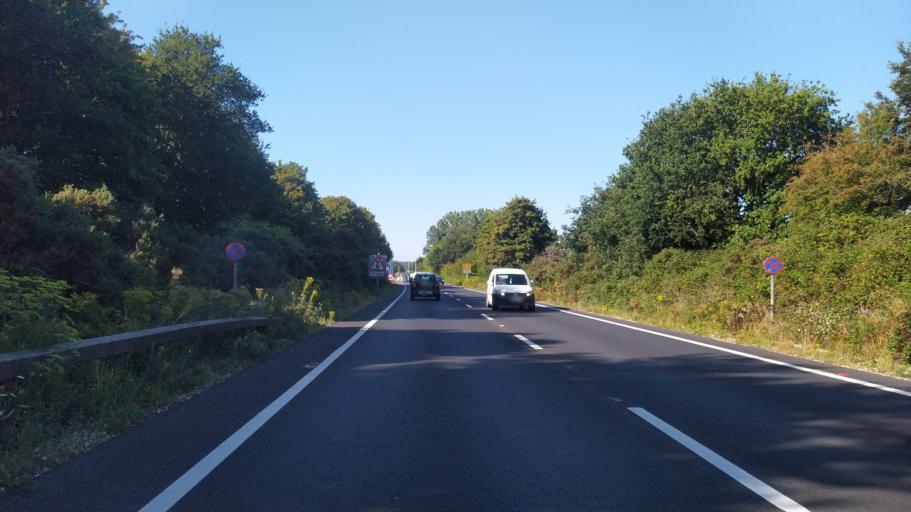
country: GB
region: England
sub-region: Dorset
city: Ferndown
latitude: 50.8058
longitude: -1.9357
